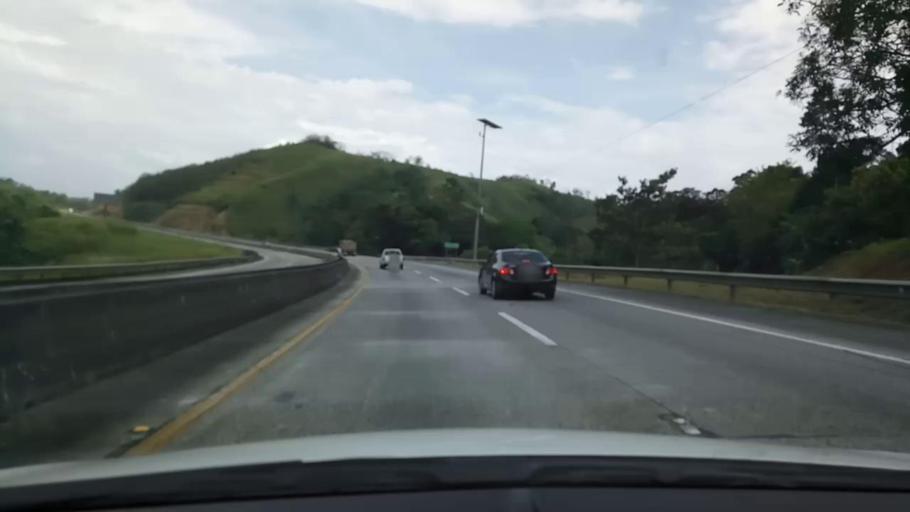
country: PA
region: Colon
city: Quebrada Bonita Adentro
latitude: 9.2752
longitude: -79.7236
